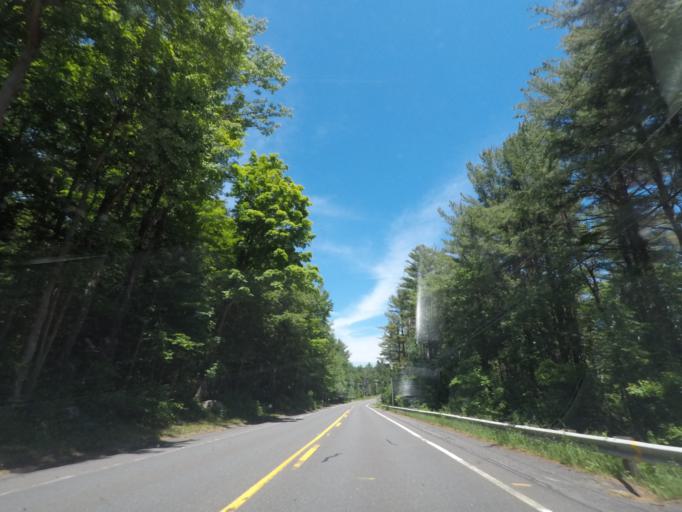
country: US
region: Massachusetts
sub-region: Berkshire County
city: Otis
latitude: 42.2555
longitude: -73.1092
